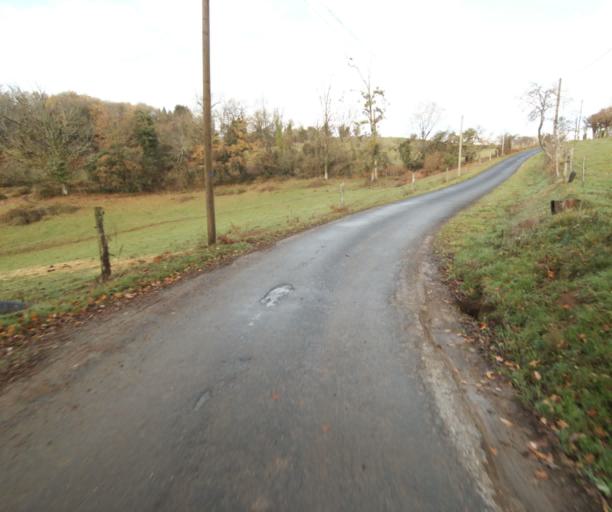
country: FR
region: Limousin
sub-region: Departement de la Correze
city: Saint-Mexant
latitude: 45.2501
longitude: 1.6335
